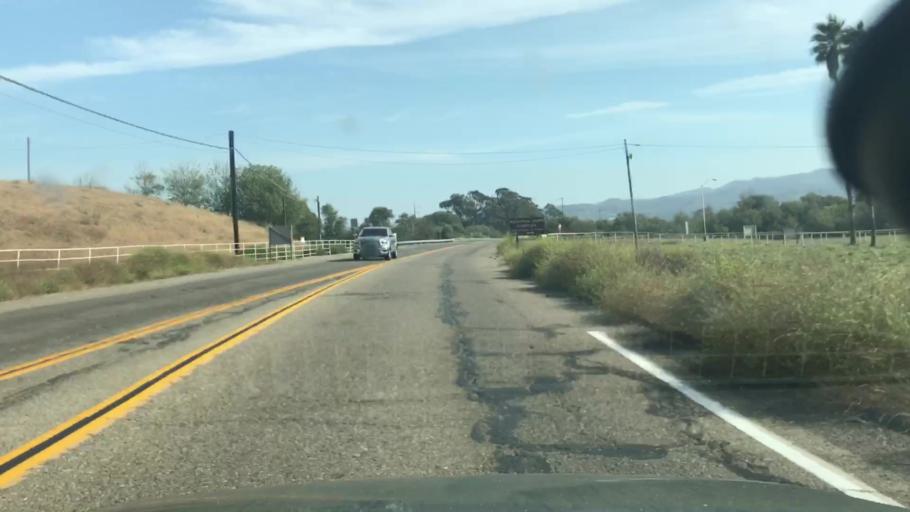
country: US
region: California
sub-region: Santa Barbara County
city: Vandenberg Village
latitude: 34.6742
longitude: -120.4940
